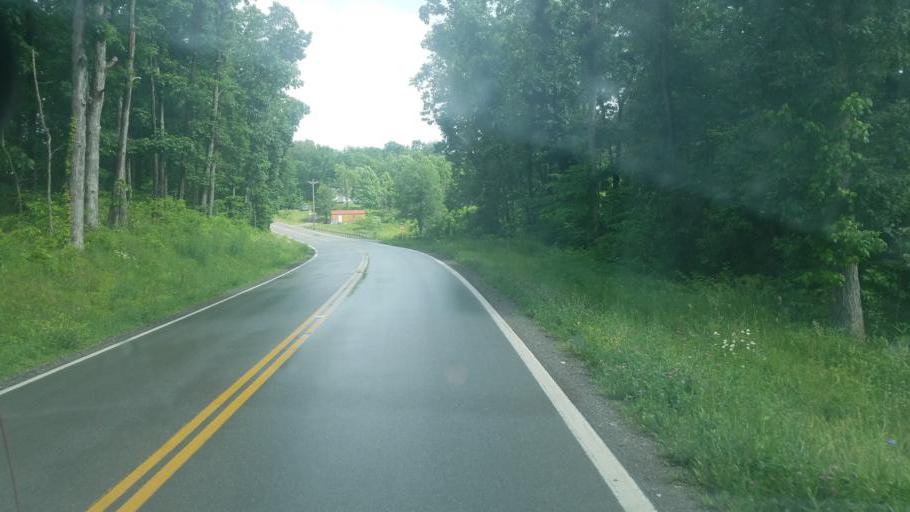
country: US
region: Ohio
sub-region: Harrison County
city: Cadiz
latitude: 40.4354
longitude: -80.9720
